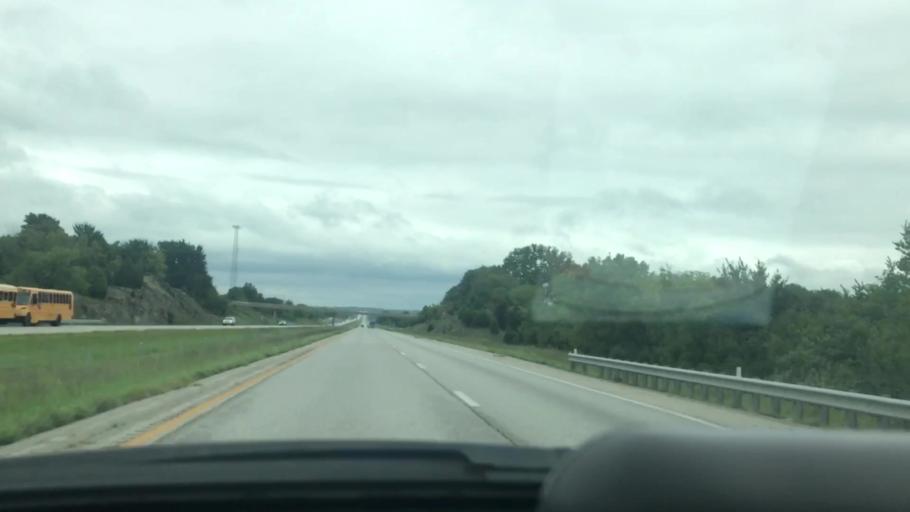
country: US
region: Missouri
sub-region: Lawrence County
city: Mount Vernon
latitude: 37.1531
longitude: -93.6991
